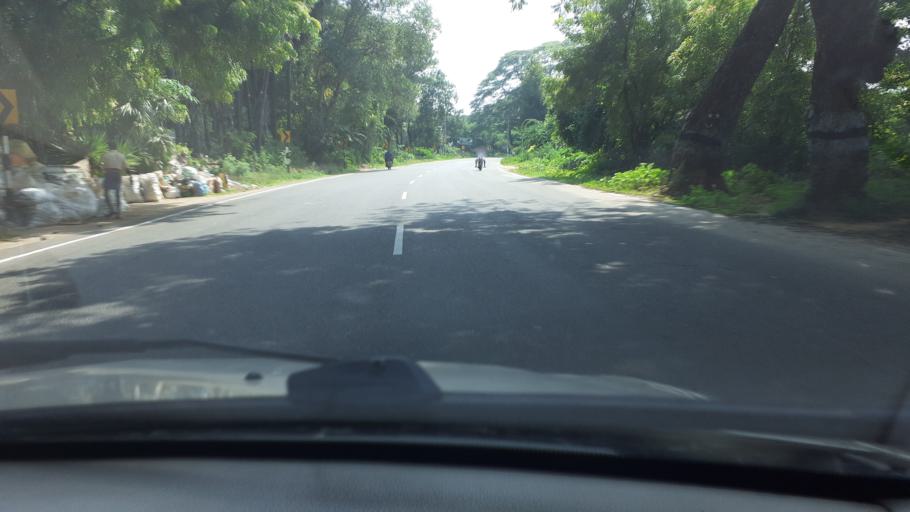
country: IN
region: Tamil Nadu
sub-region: Thoothukkudi
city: Srivaikuntam
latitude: 8.6308
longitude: 77.9041
